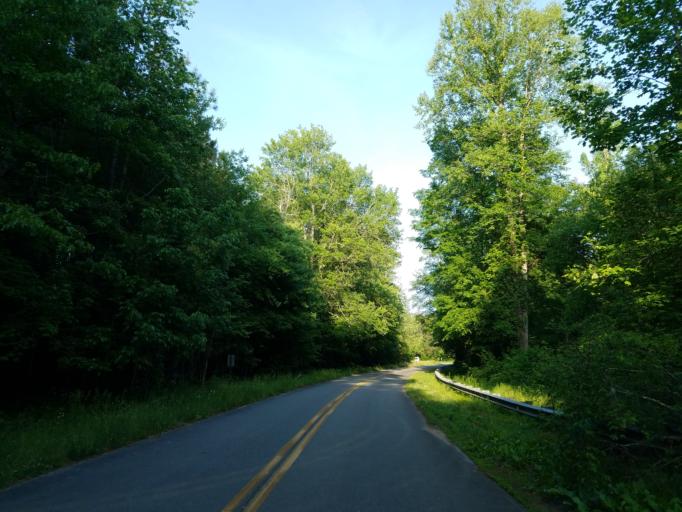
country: US
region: Georgia
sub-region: Gordon County
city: Calhoun
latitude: 34.5794
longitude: -85.0941
